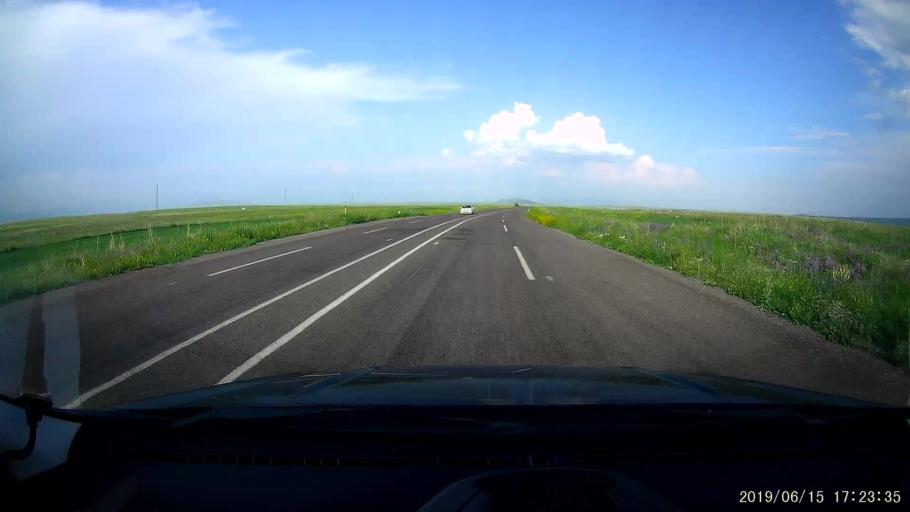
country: TR
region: Kars
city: Basgedikler
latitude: 40.6168
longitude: 43.3661
